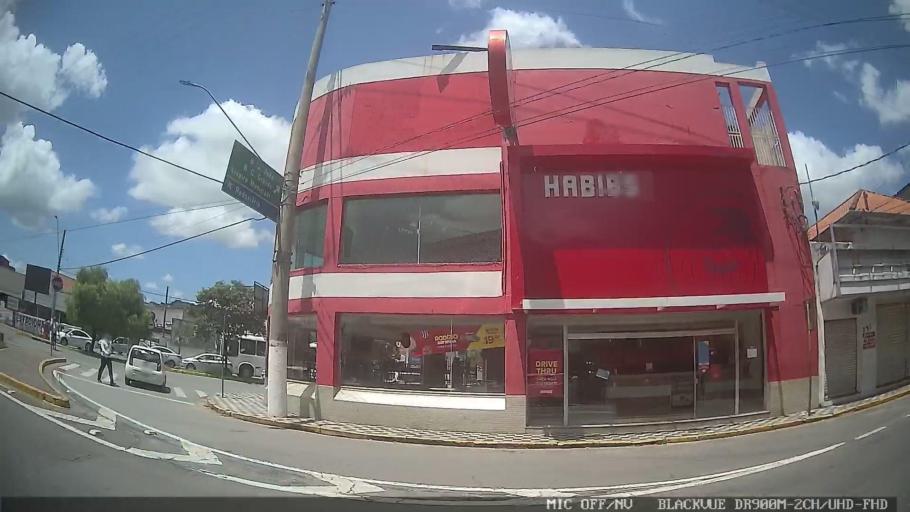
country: BR
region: Sao Paulo
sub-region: Jacarei
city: Jacarei
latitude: -23.3063
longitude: -45.9674
